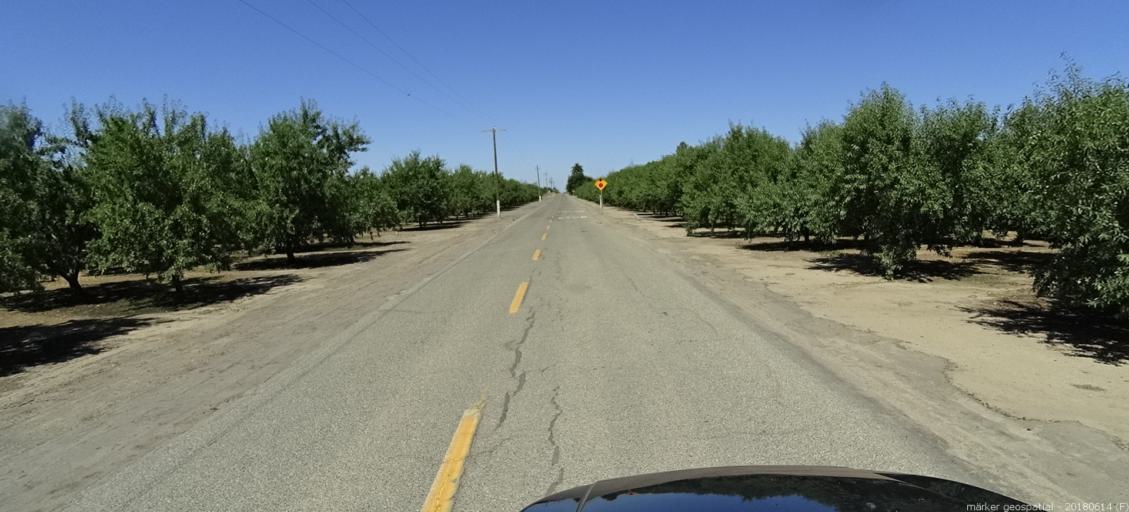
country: US
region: California
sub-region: Madera County
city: Fairmead
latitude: 36.9892
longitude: -120.1995
